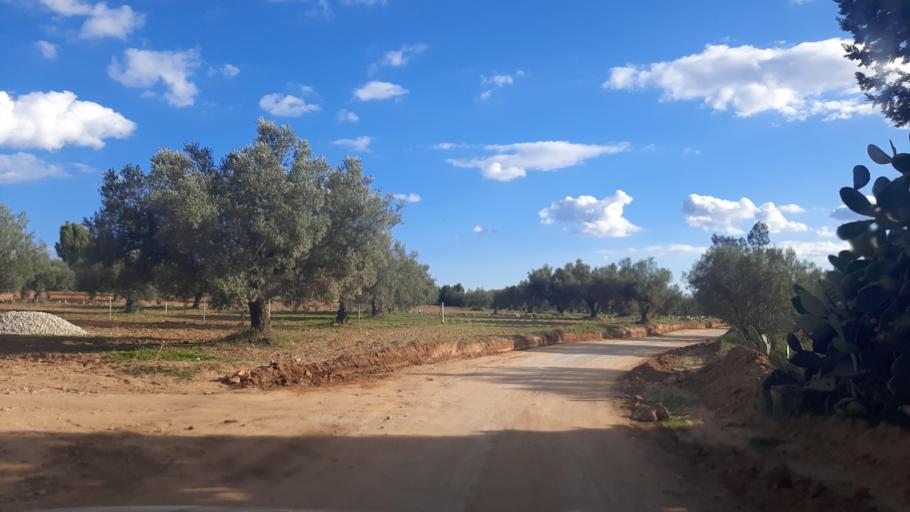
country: TN
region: Nabul
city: Al Hammamat
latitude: 36.4261
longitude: 10.5077
